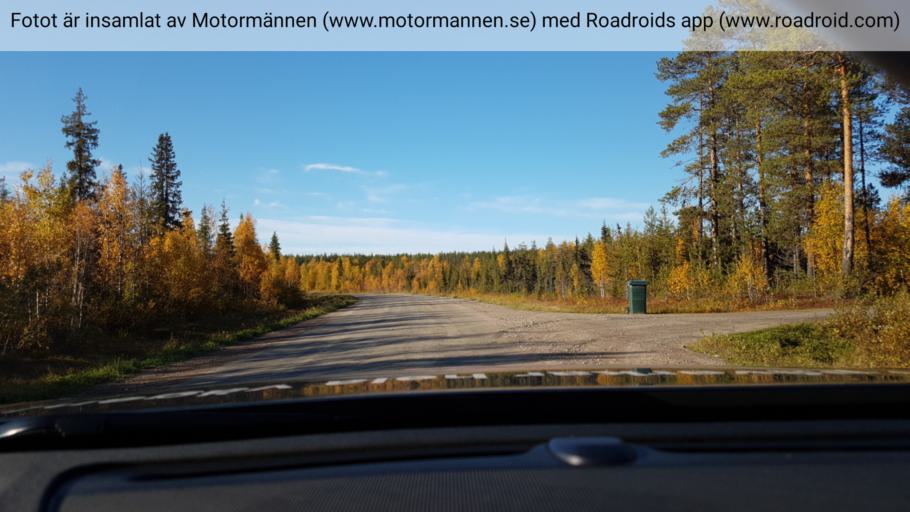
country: SE
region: Norrbotten
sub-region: Alvsbyns Kommun
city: AElvsbyn
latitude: 66.2776
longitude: 21.0965
